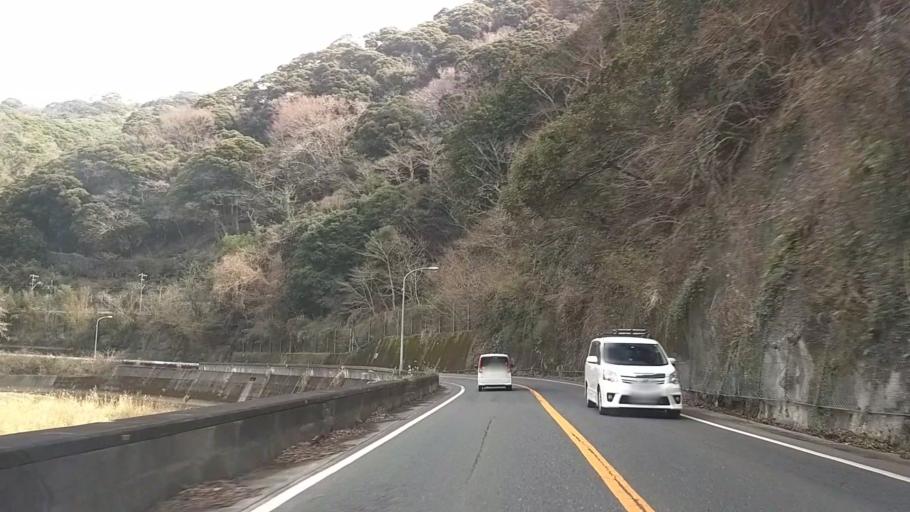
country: JP
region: Shizuoka
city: Shimoda
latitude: 34.7129
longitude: 138.9464
